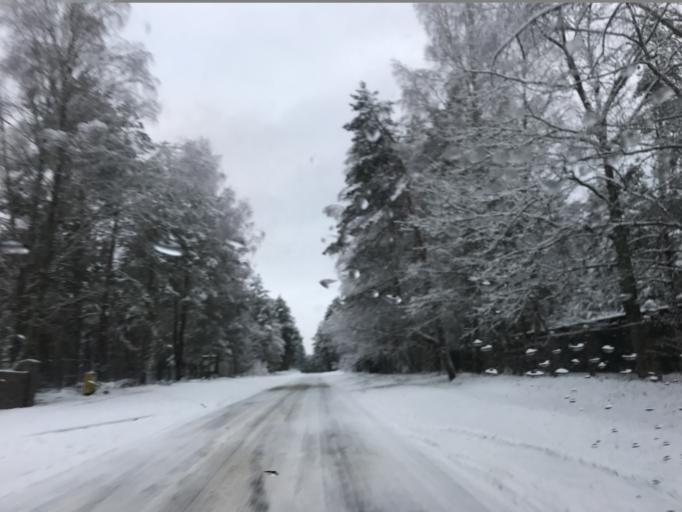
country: PL
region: Pomeranian Voivodeship
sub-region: Powiat bytowski
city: Czarna Dabrowka
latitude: 54.2761
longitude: 17.5889
